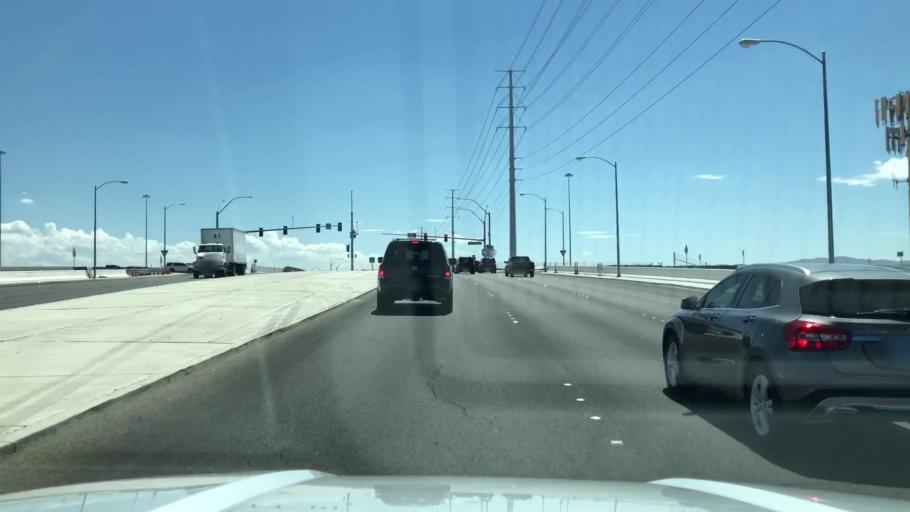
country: US
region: Nevada
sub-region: Clark County
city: Spring Valley
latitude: 36.0685
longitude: -115.2795
